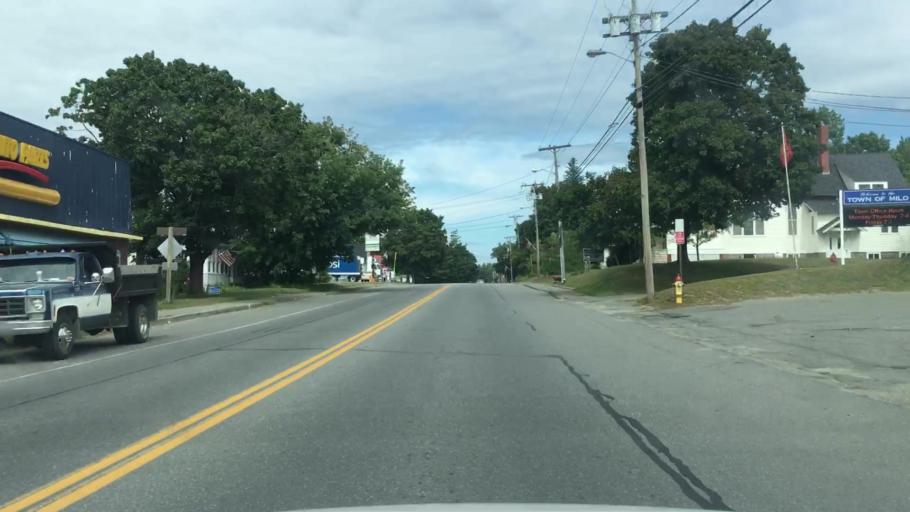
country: US
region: Maine
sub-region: Piscataquis County
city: Milo
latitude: 45.2536
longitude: -68.9863
